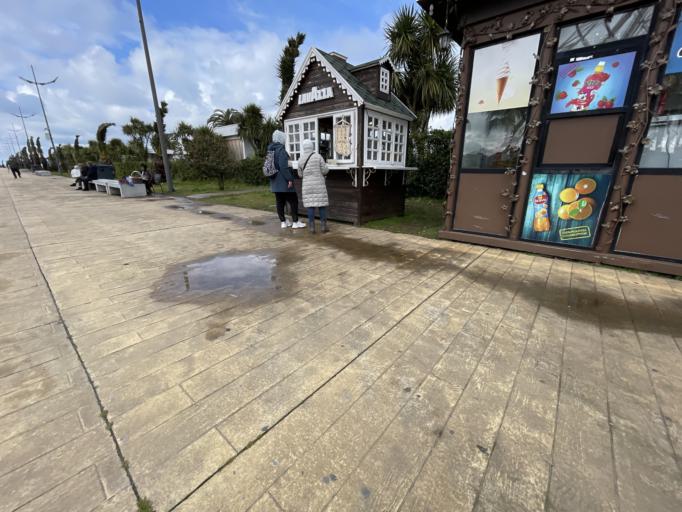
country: GE
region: Ajaria
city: Batumi
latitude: 41.6557
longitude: 41.6427
